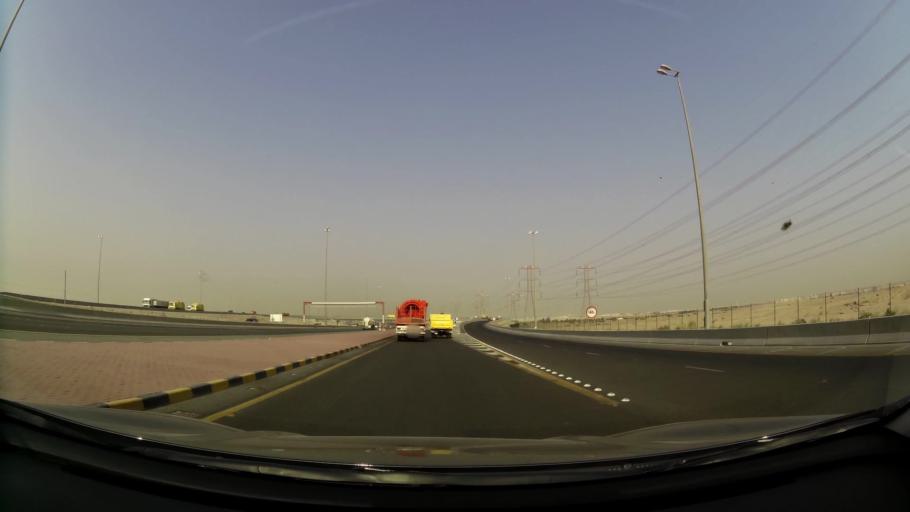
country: KW
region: Al Asimah
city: Ar Rabiyah
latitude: 29.2506
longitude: 47.8682
